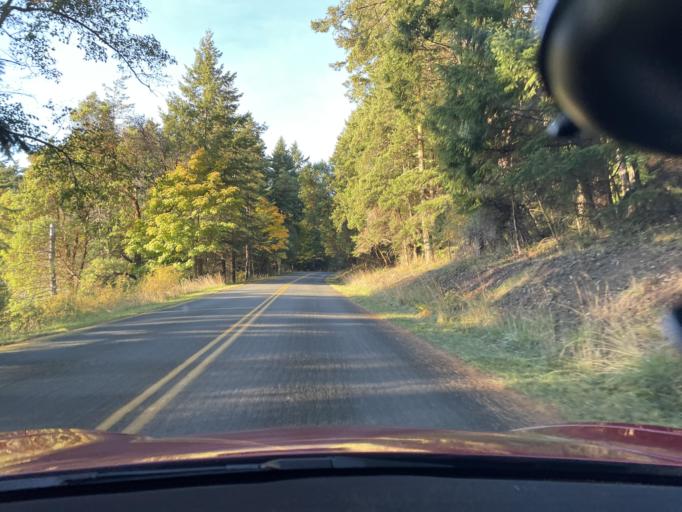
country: US
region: Washington
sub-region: San Juan County
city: Friday Harbor
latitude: 48.5426
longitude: -123.1587
